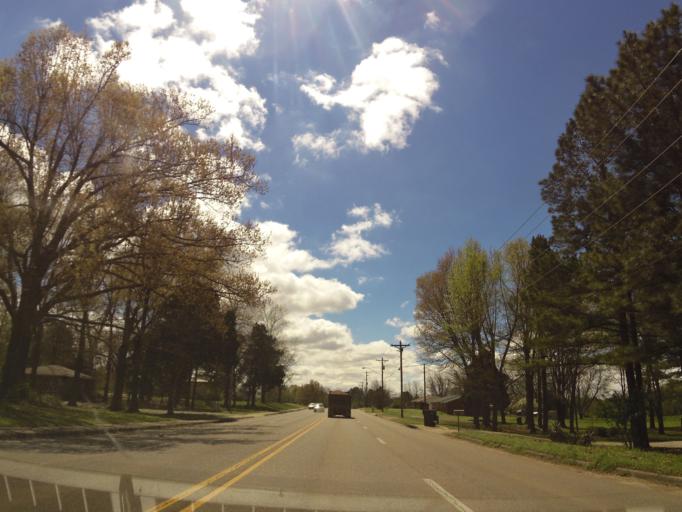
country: US
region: Arkansas
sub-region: Craighead County
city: Jonesboro
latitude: 35.8736
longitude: -90.7028
